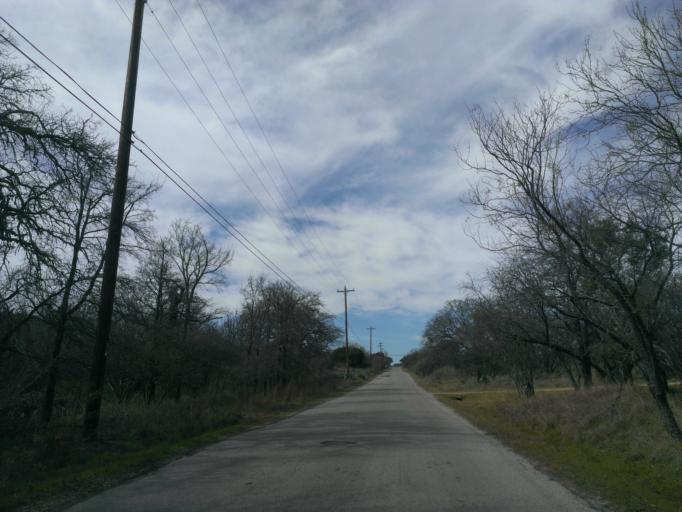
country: US
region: Texas
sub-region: Burnet County
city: Granite Shoals
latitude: 30.5786
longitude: -98.3913
